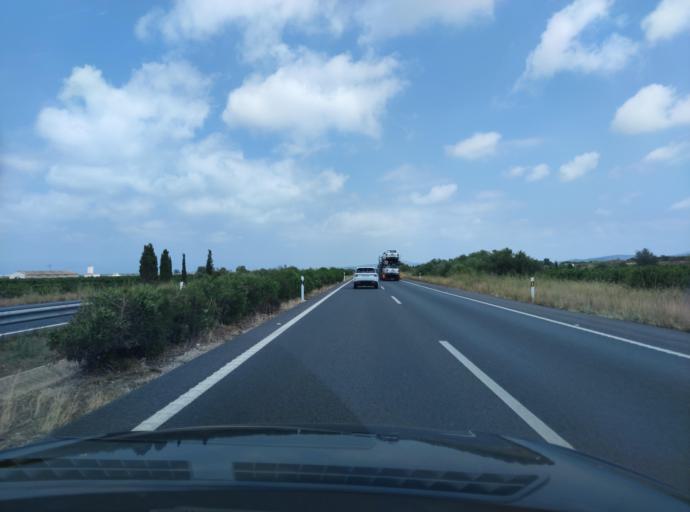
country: ES
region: Catalonia
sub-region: Provincia de Tarragona
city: Alcanar
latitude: 40.5134
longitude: 0.4154
